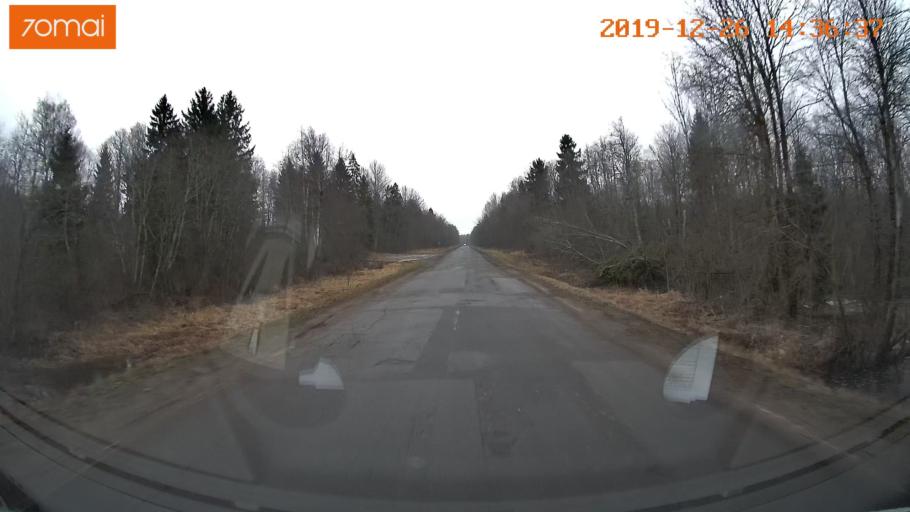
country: RU
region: Jaroslavl
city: Poshekhon'ye
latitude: 58.4097
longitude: 38.9754
